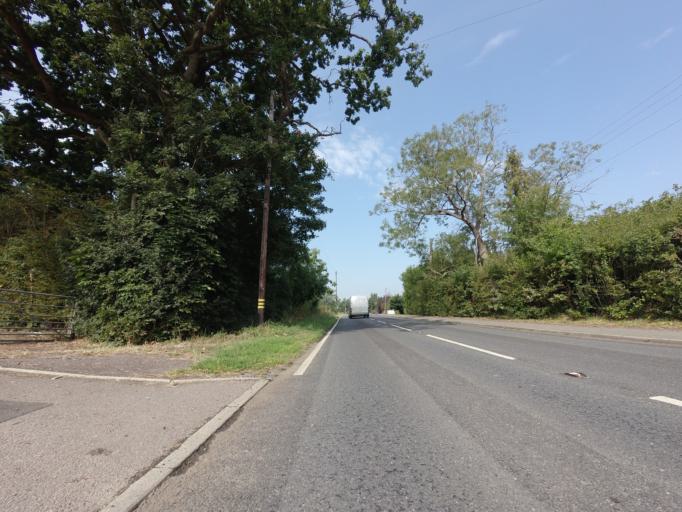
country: GB
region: England
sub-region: Kent
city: Headcorn
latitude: 51.1150
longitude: 0.6334
